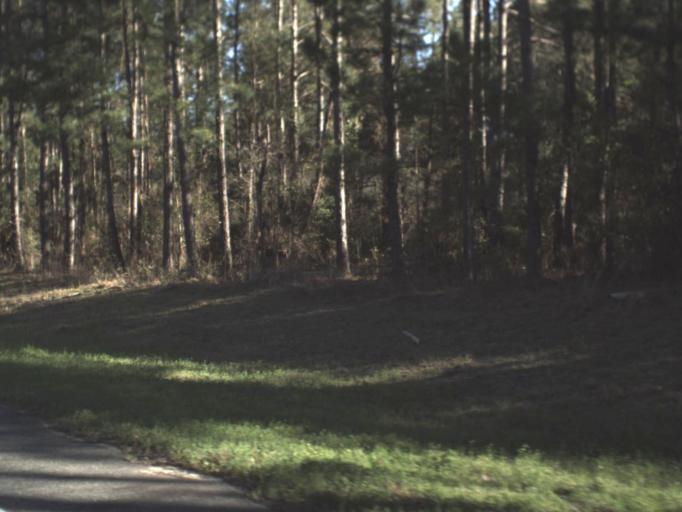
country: US
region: Georgia
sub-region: Brooks County
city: Quitman
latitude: 30.6010
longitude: -83.6439
